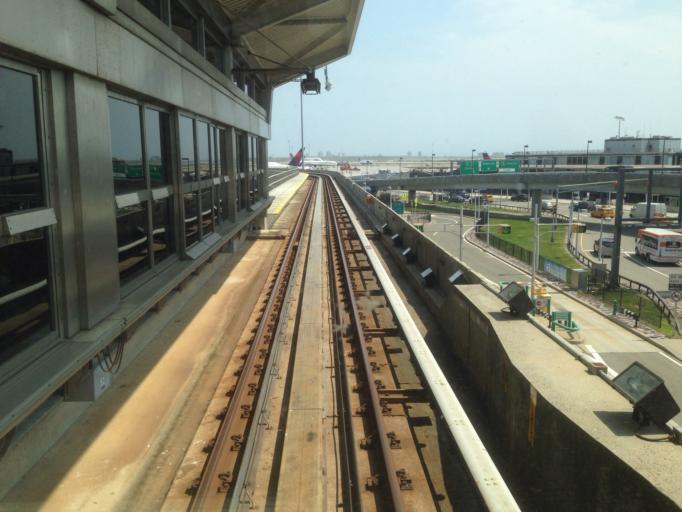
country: US
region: New York
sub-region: Nassau County
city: Inwood
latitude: 40.6436
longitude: -73.7889
